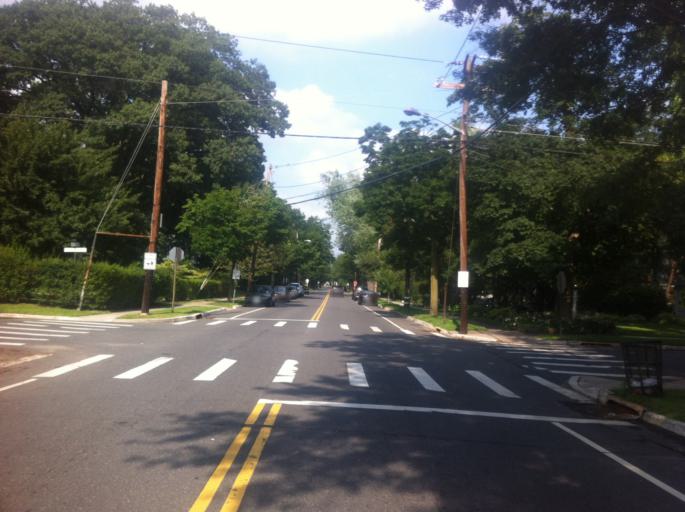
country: US
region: New York
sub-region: Nassau County
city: Sea Cliff
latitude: 40.8474
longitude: -73.6438
